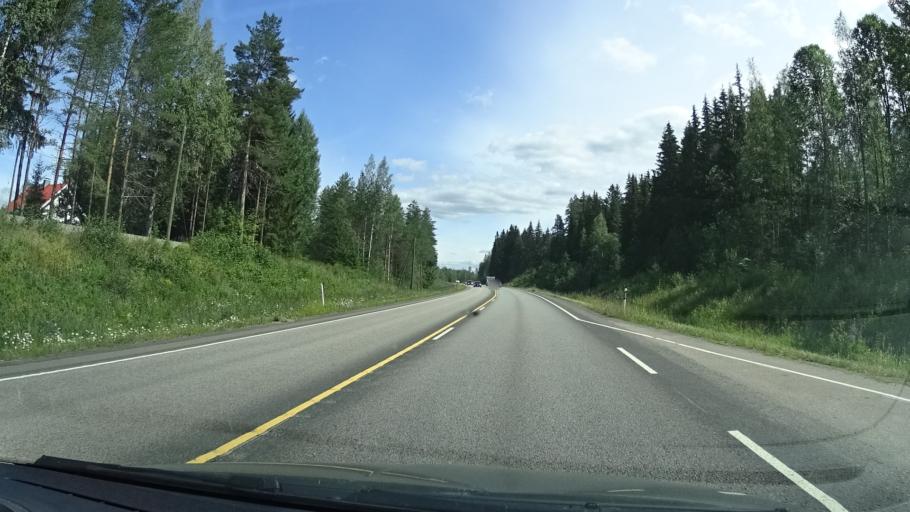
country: FI
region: Central Finland
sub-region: Jyvaeskylae
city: Muurame
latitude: 62.2667
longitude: 25.5015
